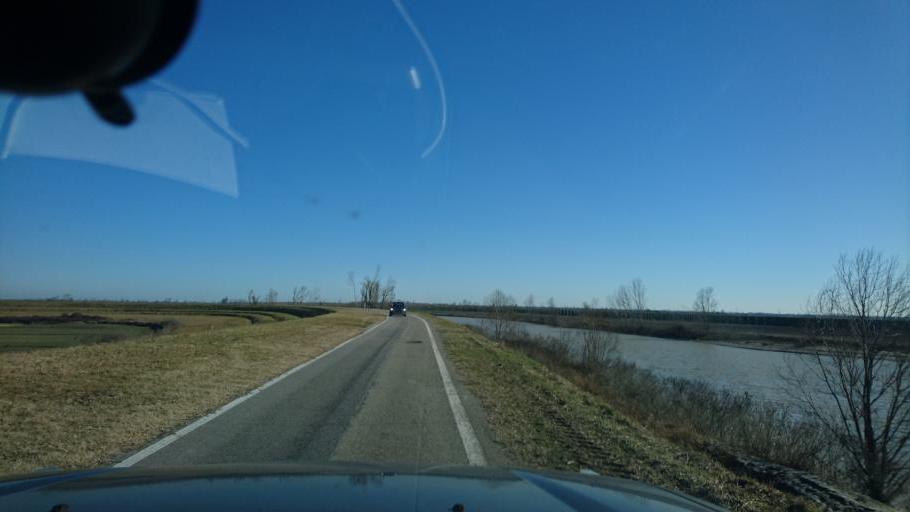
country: IT
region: Veneto
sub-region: Provincia di Rovigo
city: Ariano
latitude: 44.9316
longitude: 12.1533
